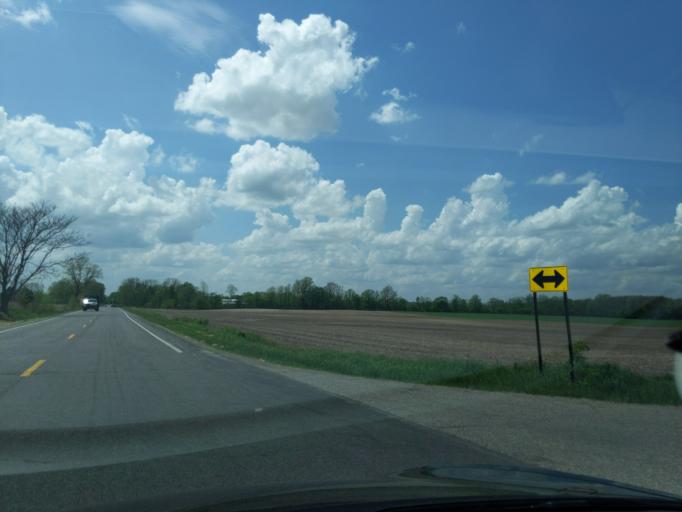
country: US
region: Michigan
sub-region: Ingham County
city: Mason
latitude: 42.5963
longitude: -84.3836
